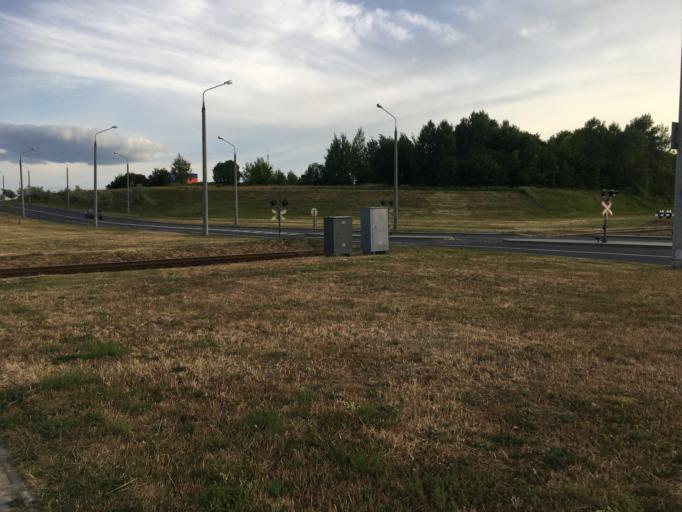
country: BY
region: Grodnenskaya
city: Hrodna
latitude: 53.7192
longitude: 23.8403
